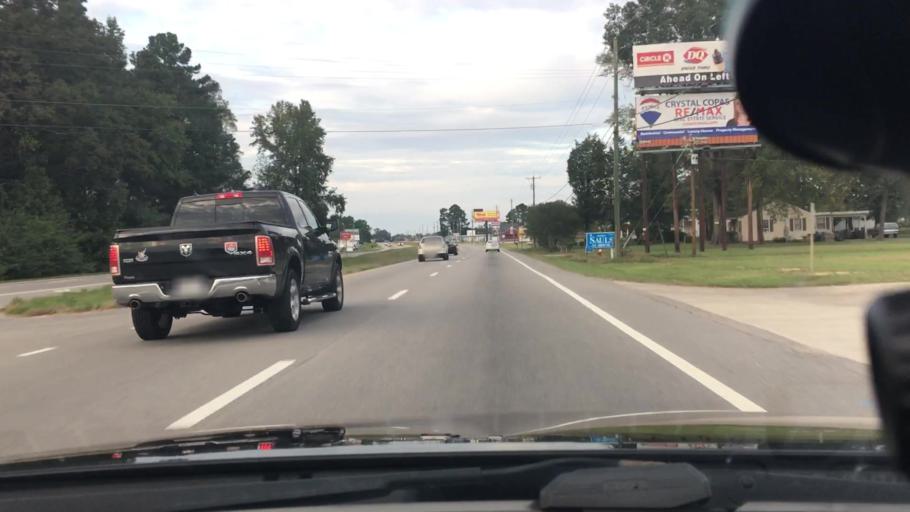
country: US
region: North Carolina
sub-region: Lee County
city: Sanford
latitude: 35.4283
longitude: -79.2225
